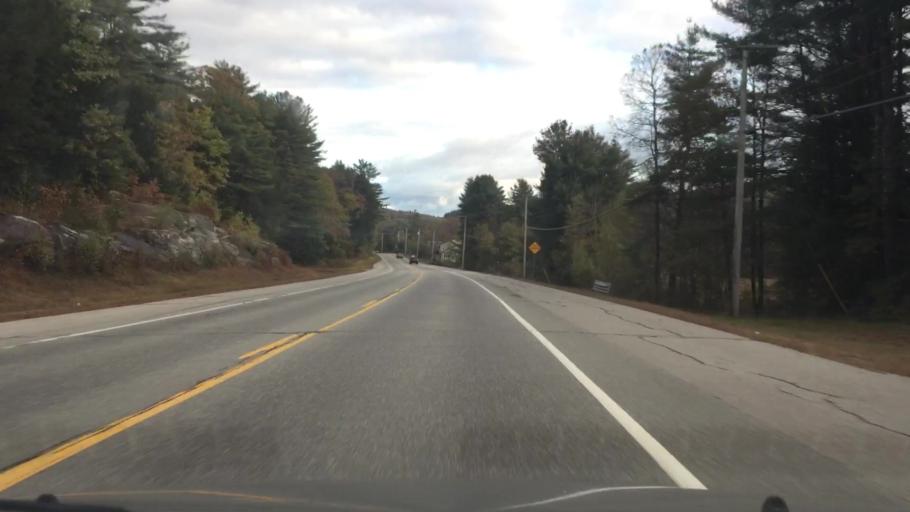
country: US
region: New Hampshire
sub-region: Cheshire County
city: Keene
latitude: 42.9985
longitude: -72.2588
